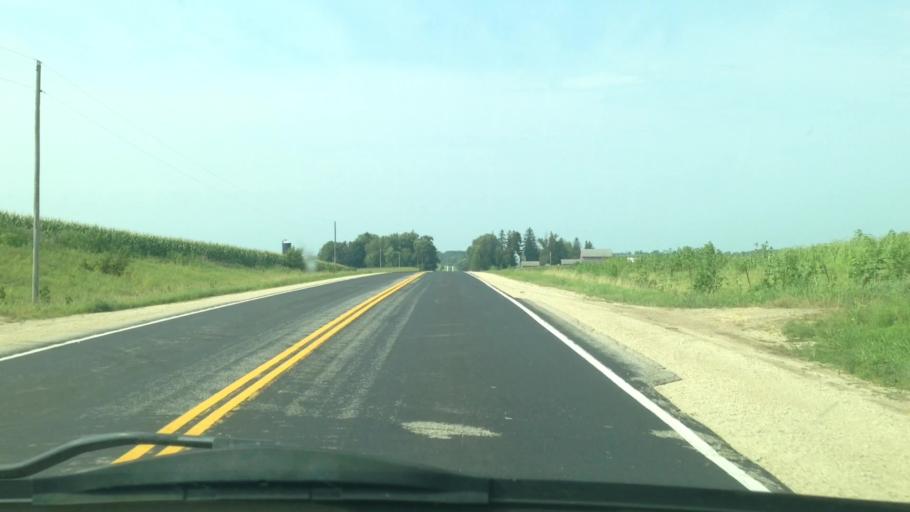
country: US
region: Minnesota
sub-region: Winona County
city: Lewiston
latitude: 43.9029
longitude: -91.9594
